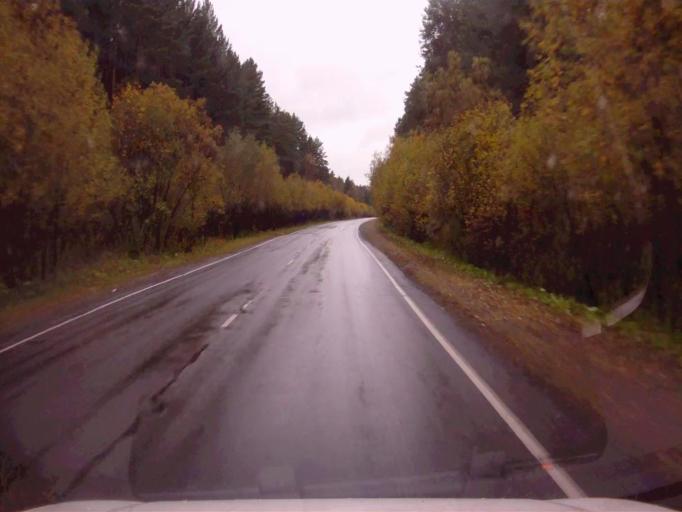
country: RU
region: Chelyabinsk
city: Verkhniy Ufaley
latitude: 56.0493
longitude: 60.1484
